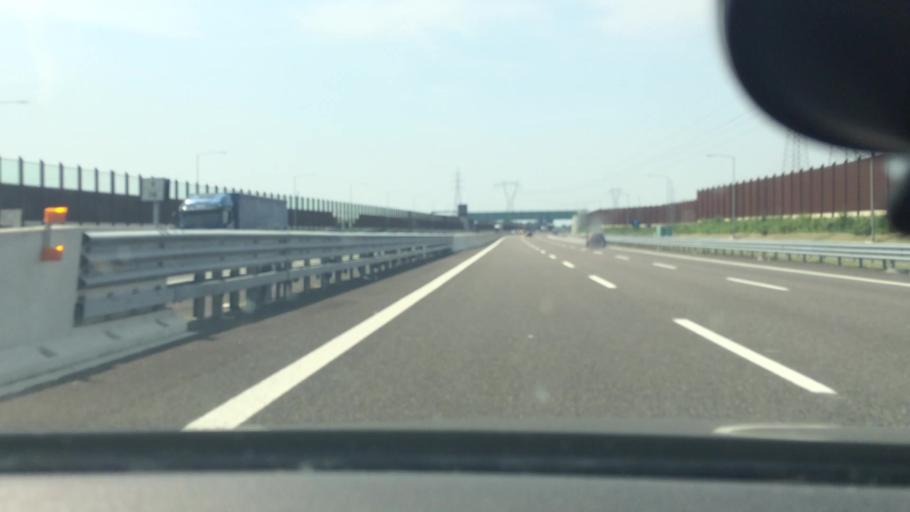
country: IT
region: Lombardy
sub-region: Provincia di Lodi
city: Zelo Buon Persico
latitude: 45.4205
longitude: 9.4191
